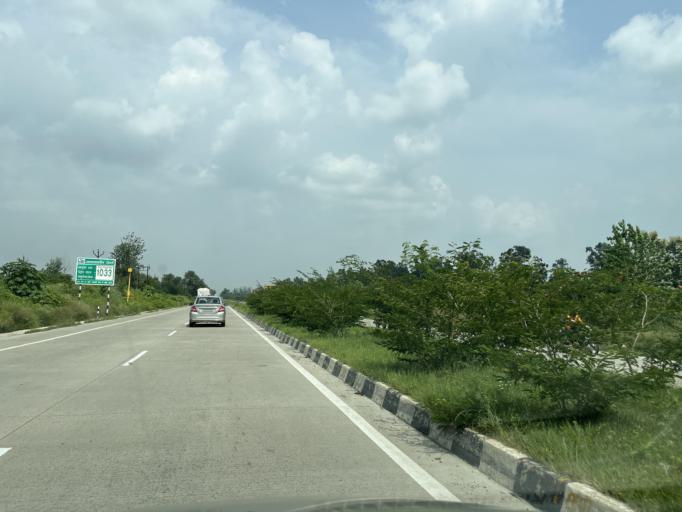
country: IN
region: Uttar Pradesh
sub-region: Bijnor
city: Sherkot
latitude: 29.3214
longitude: 78.5561
